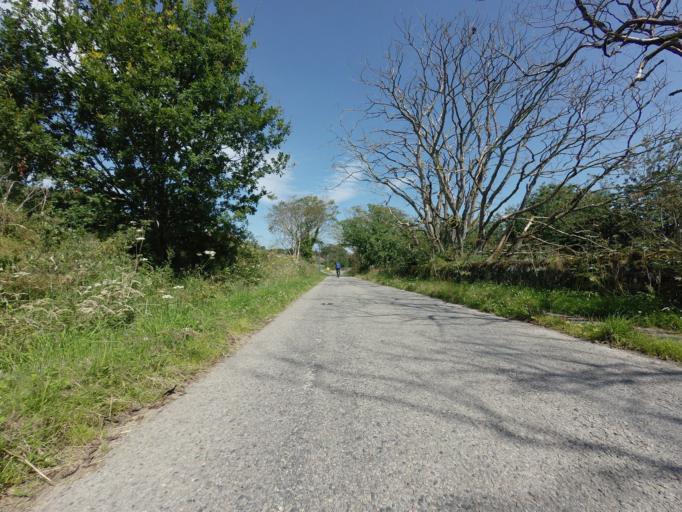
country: GB
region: Scotland
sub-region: Highland
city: Dingwall
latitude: 57.5841
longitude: -4.4323
